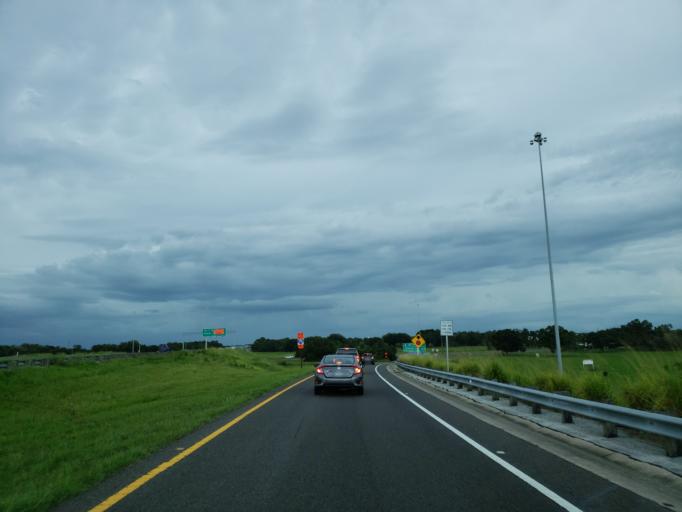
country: US
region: Florida
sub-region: Manatee County
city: Memphis
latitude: 27.5850
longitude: -82.5439
